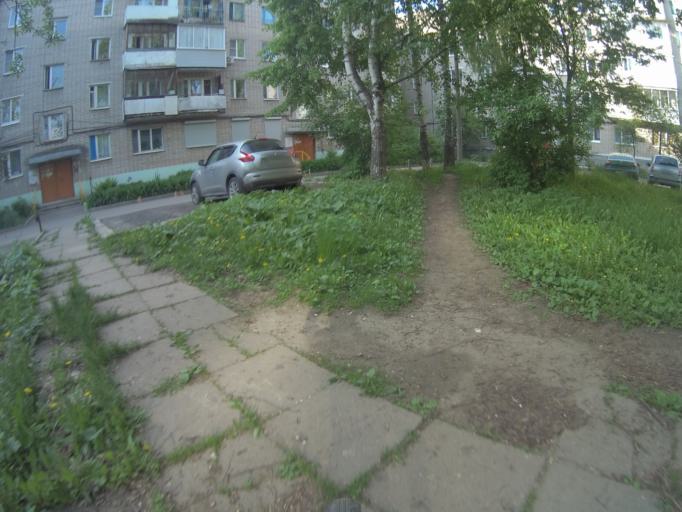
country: RU
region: Vladimir
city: Bogolyubovo
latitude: 56.1680
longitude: 40.4769
